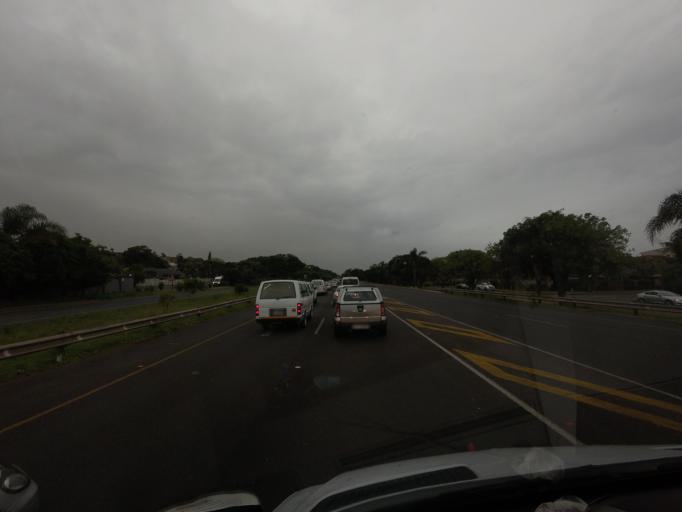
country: ZA
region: KwaZulu-Natal
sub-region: eThekwini Metropolitan Municipality
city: Durban
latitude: -29.7176
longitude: 31.0878
